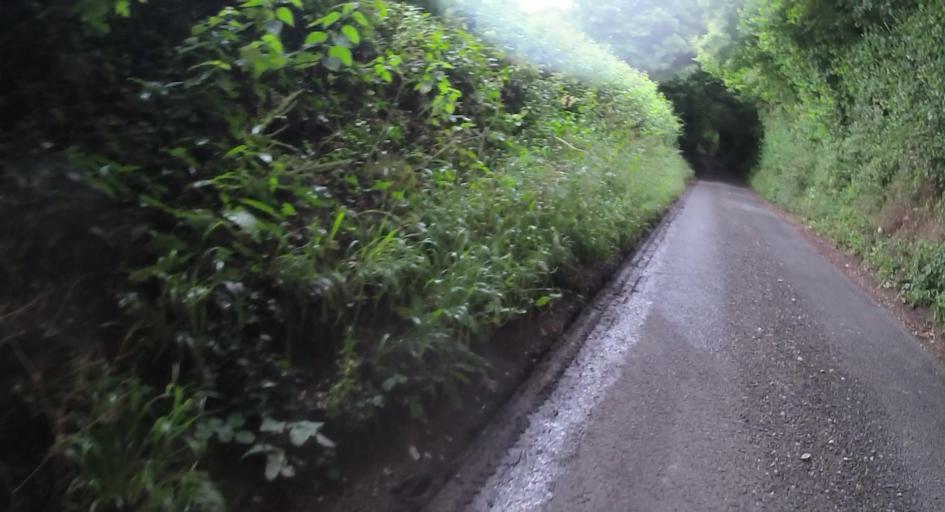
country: GB
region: England
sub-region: Hampshire
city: Long Sutton
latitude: 51.1980
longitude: -0.9138
